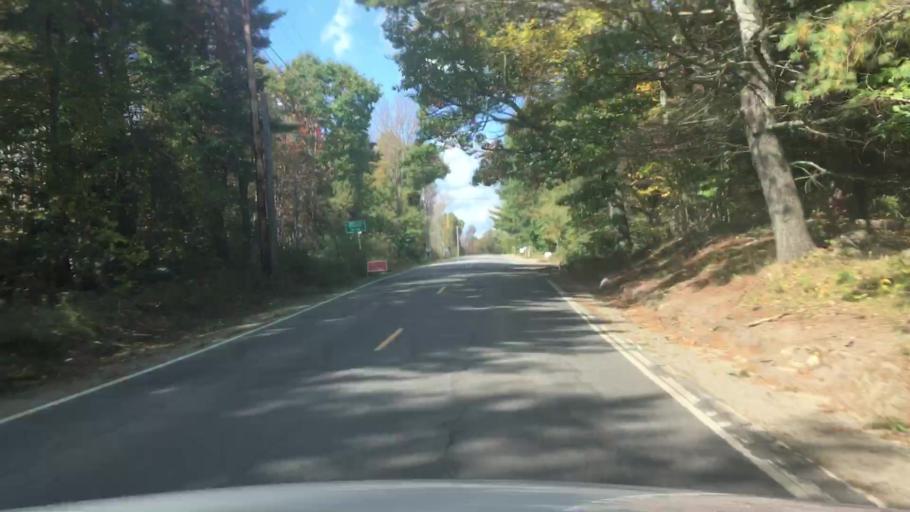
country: US
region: Maine
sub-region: Knox County
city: Union
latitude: 44.1808
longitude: -69.2593
